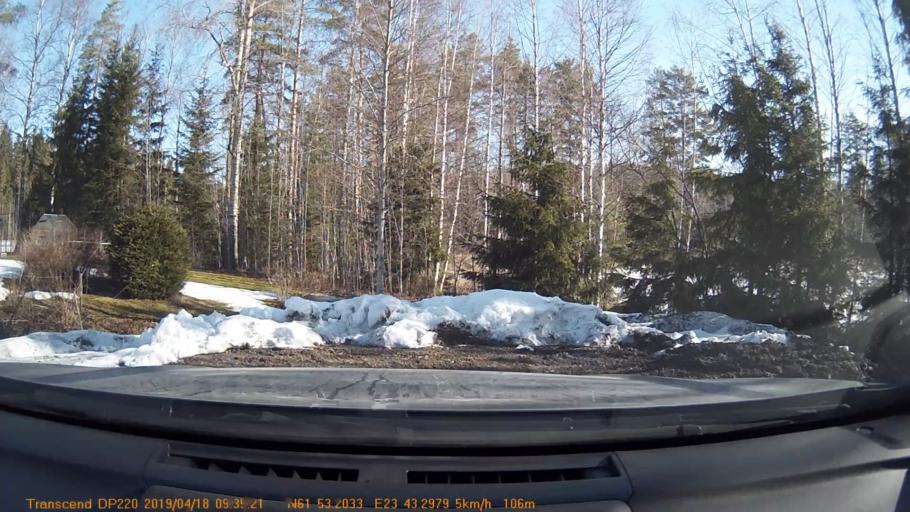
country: FI
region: Pirkanmaa
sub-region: Tampere
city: Kuru
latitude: 61.8867
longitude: 23.7216
